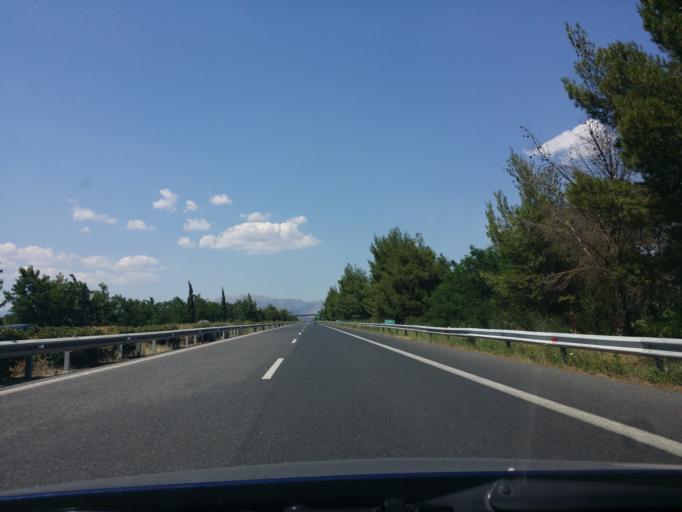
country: GR
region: Peloponnese
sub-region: Nomos Arkadias
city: Tripoli
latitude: 37.5298
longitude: 22.4112
